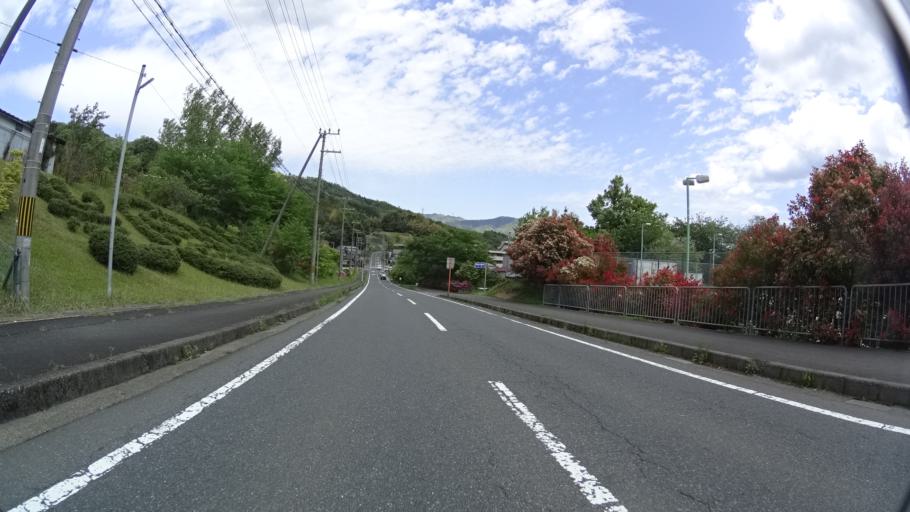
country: JP
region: Kyoto
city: Miyazu
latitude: 35.5664
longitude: 135.1471
